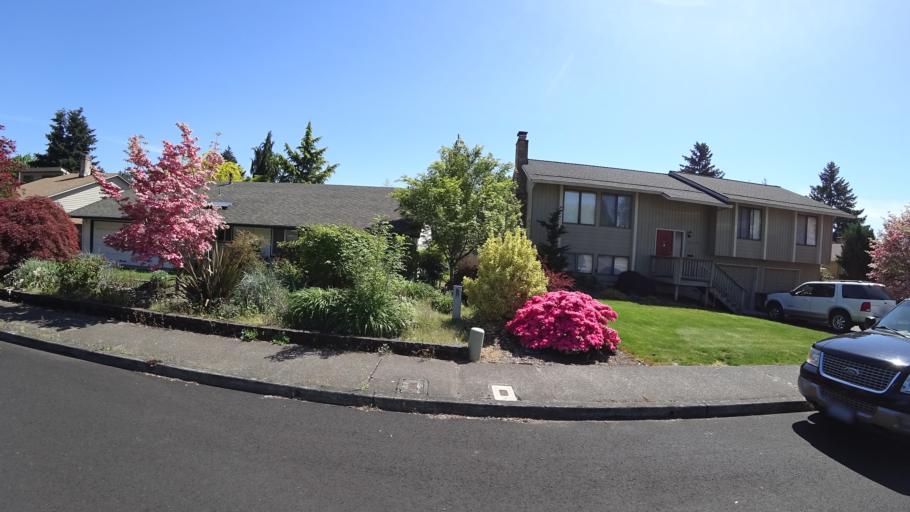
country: US
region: Oregon
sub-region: Washington County
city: Hillsboro
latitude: 45.5101
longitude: -122.9553
